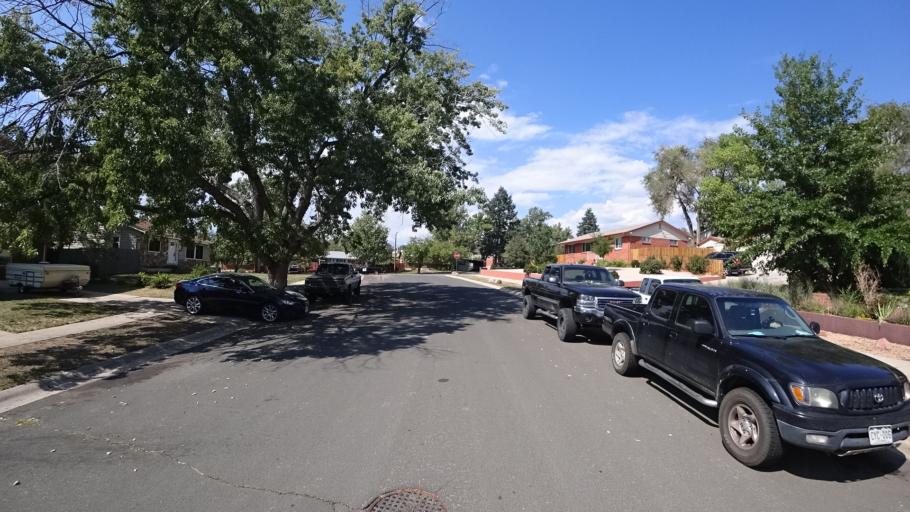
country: US
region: Colorado
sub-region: El Paso County
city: Colorado Springs
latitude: 38.8305
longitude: -104.7792
